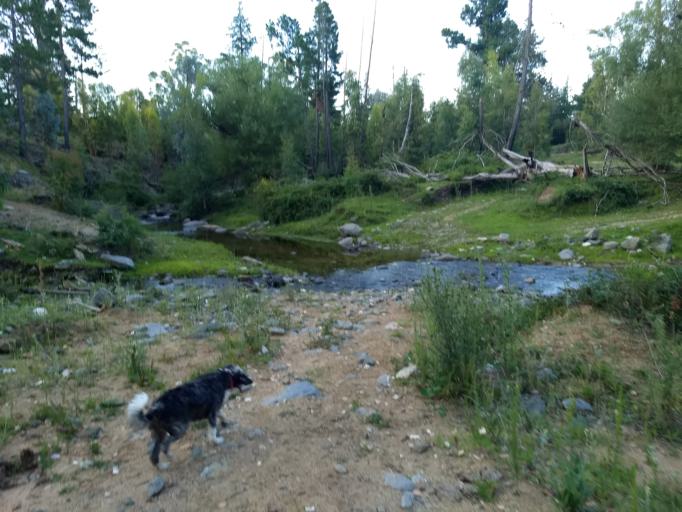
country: AR
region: Cordoba
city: Villa Berna
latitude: -31.9878
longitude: -64.8060
